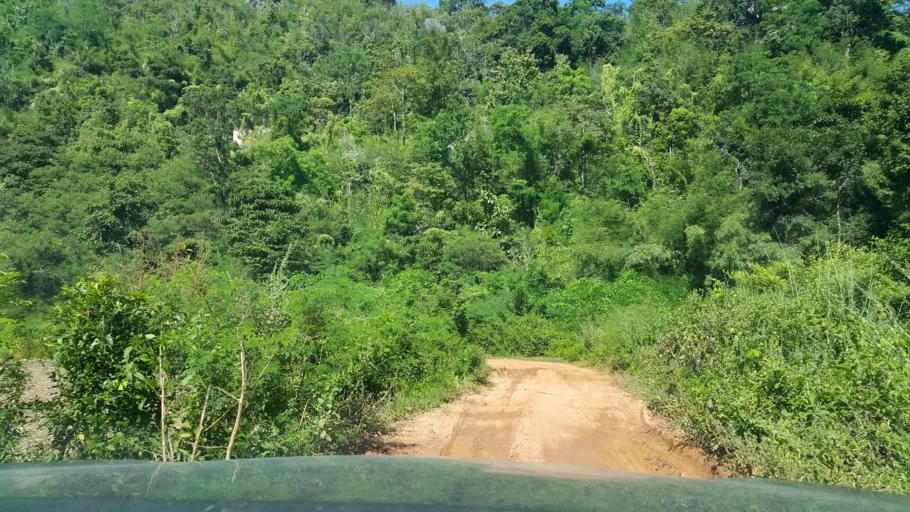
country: TH
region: Sukhothai
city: Thung Saliam
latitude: 17.3354
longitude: 99.5080
